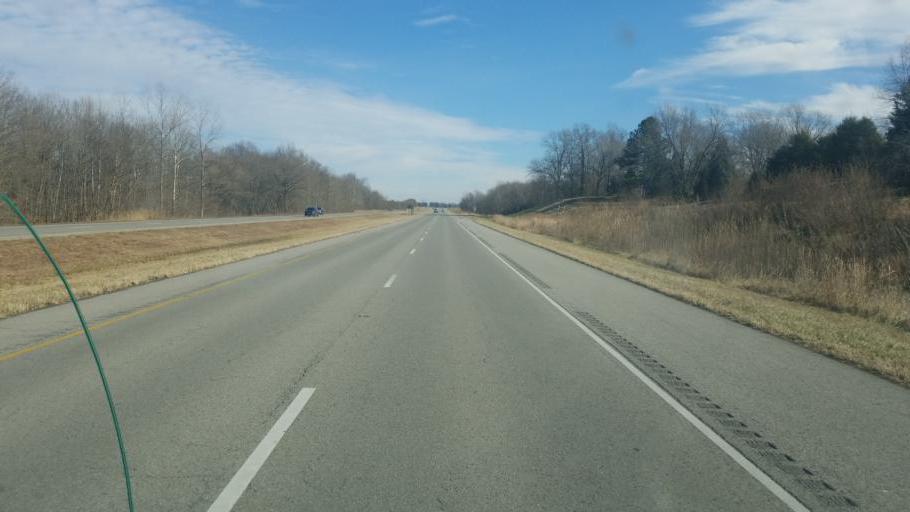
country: US
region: Illinois
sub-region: Williamson County
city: Marion
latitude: 37.7327
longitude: -88.8107
